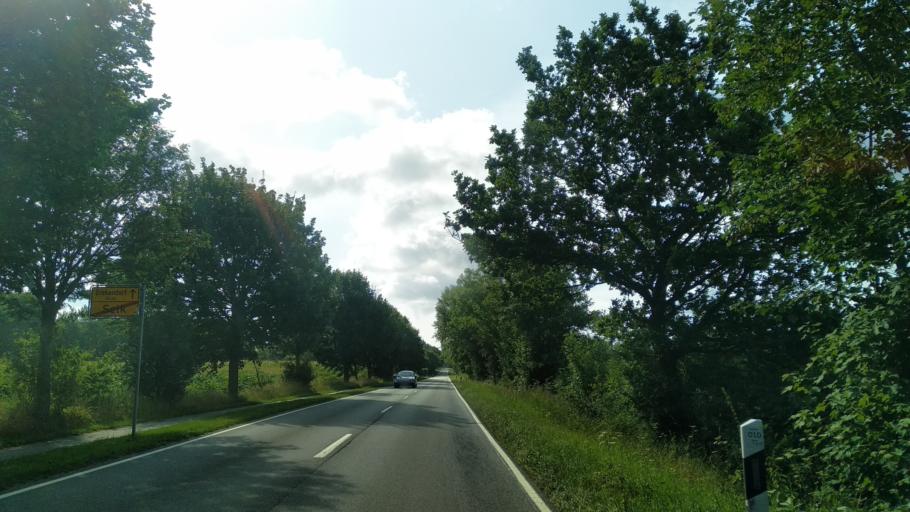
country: DE
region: Schleswig-Holstein
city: Selk
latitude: 54.4689
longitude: 9.5718
